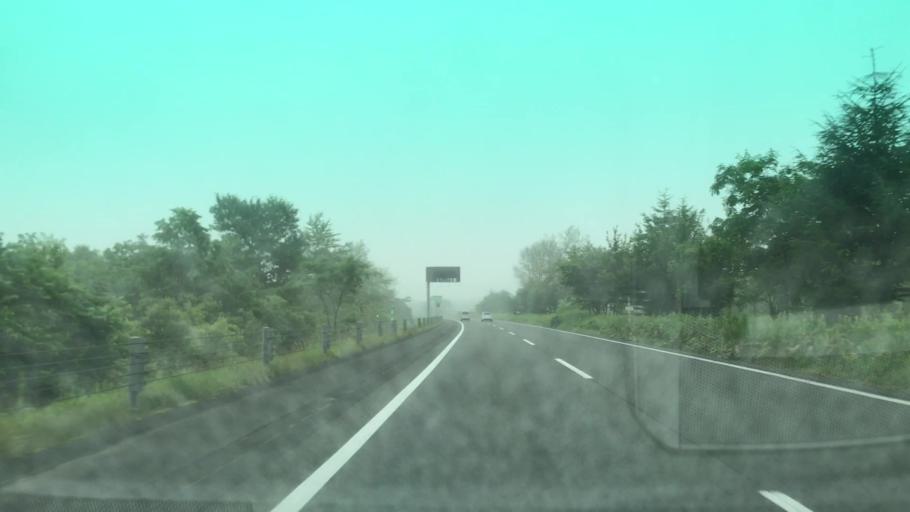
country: JP
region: Hokkaido
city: Chitose
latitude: 42.7824
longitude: 141.6266
